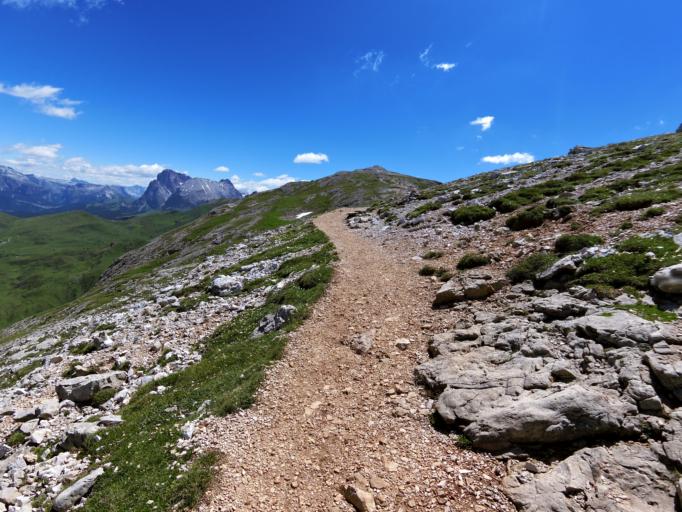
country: IT
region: Trentino-Alto Adige
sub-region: Bolzano
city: Siusi
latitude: 46.5021
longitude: 11.6016
